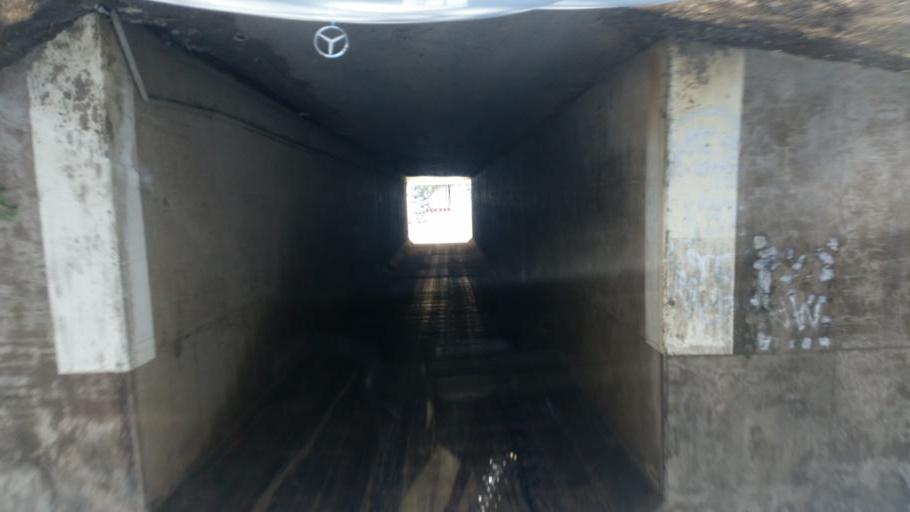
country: ZA
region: KwaZulu-Natal
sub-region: uMgungundlovu District Municipality
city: Camperdown
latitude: -29.7028
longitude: 30.4920
